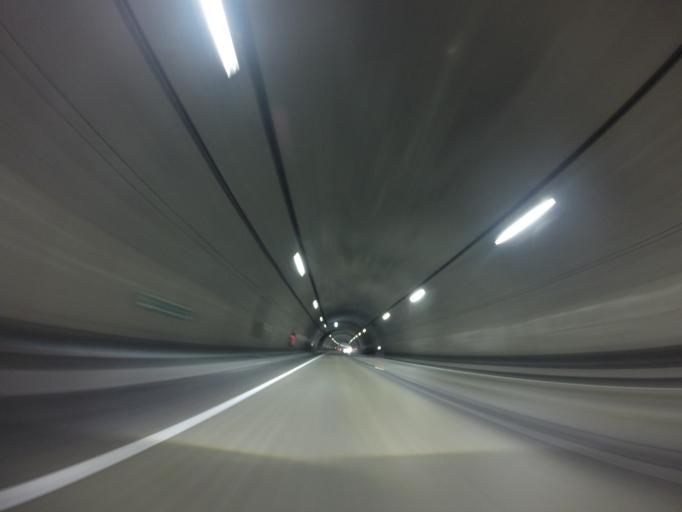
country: JP
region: Shizuoka
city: Ito
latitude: 34.9673
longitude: 138.9371
